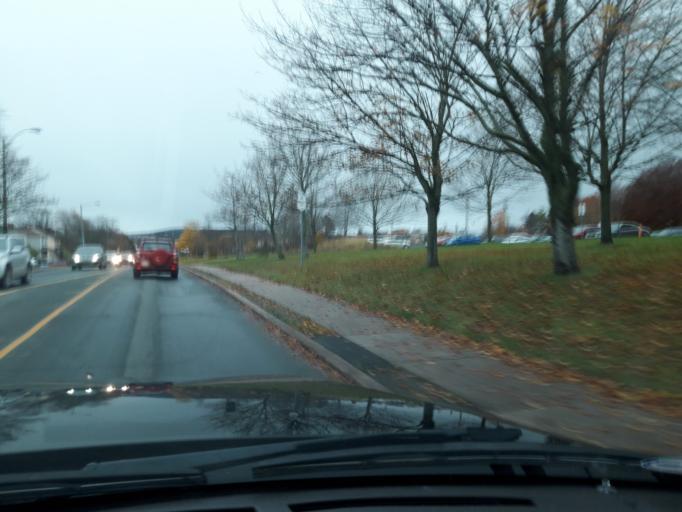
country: CA
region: Newfoundland and Labrador
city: St. John's
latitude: 47.5685
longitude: -52.7344
